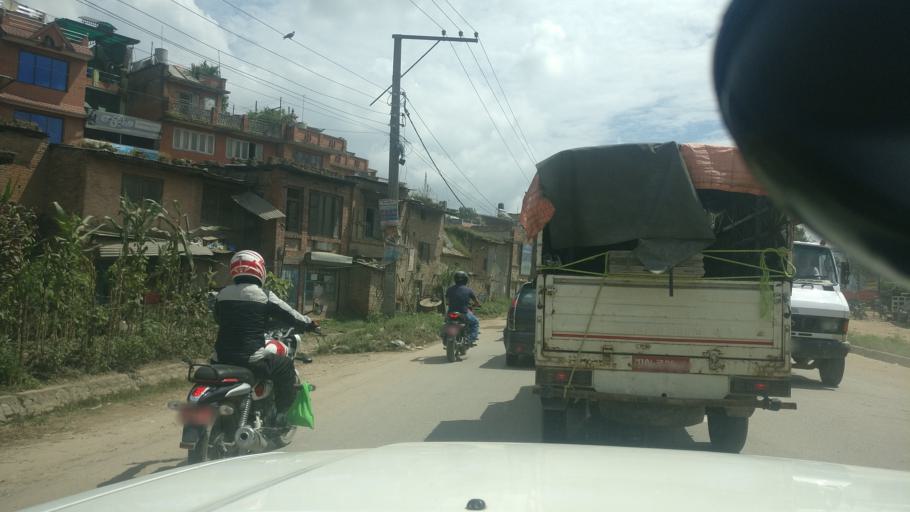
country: NP
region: Central Region
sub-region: Bagmati Zone
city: Bhaktapur
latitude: 27.6665
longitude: 85.4370
